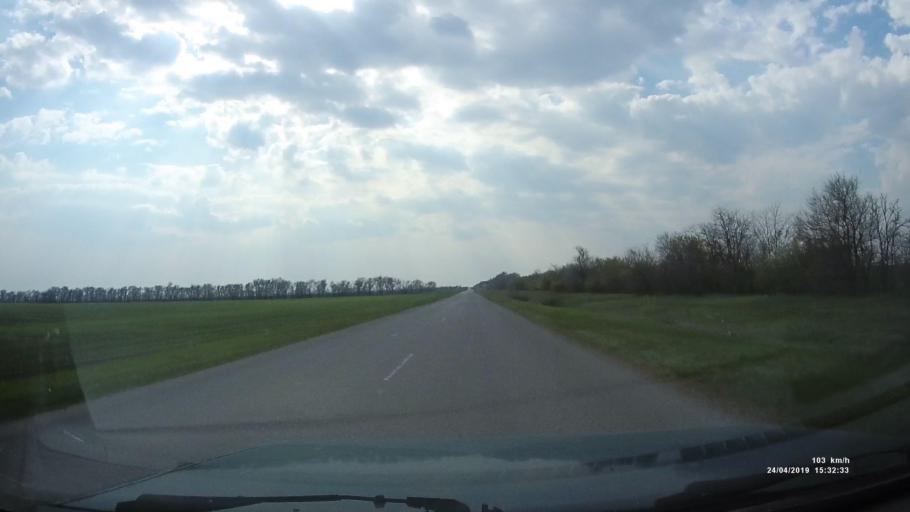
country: RU
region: Rostov
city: Remontnoye
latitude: 46.5996
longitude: 42.9576
